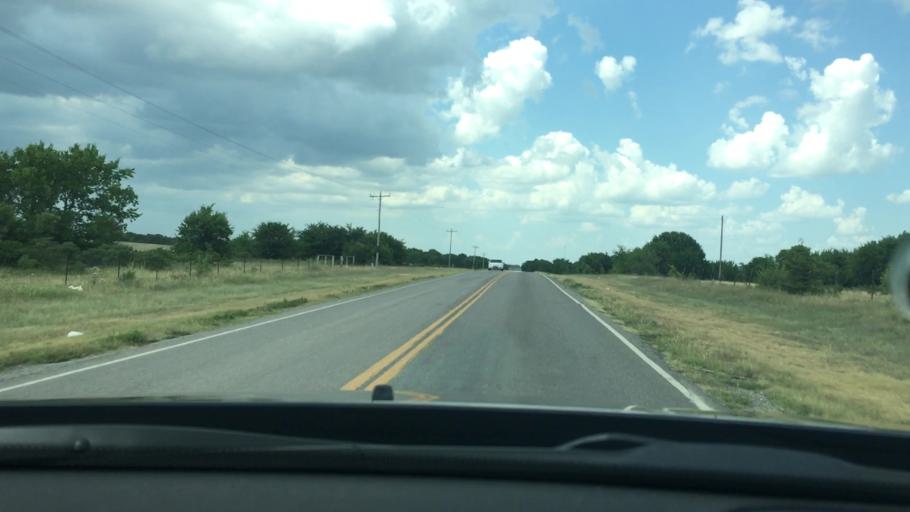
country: US
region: Oklahoma
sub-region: Pontotoc County
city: Ada
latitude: 34.5384
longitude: -96.6346
